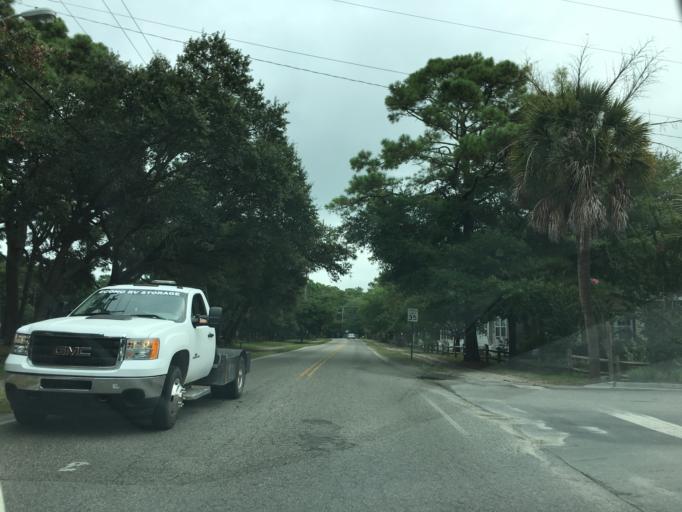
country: US
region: South Carolina
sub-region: Horry County
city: North Myrtle Beach
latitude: 33.7776
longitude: -78.7738
